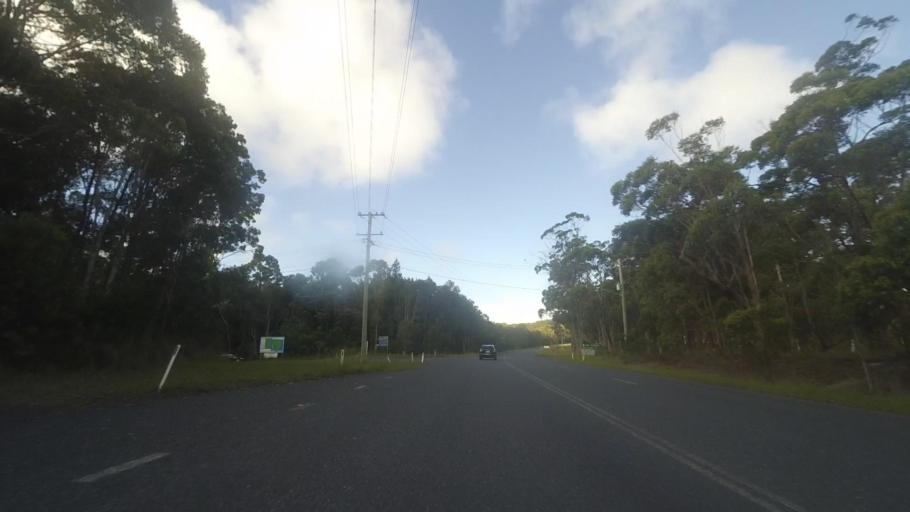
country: AU
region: New South Wales
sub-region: Great Lakes
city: Forster
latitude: -32.3554
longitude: 152.5055
